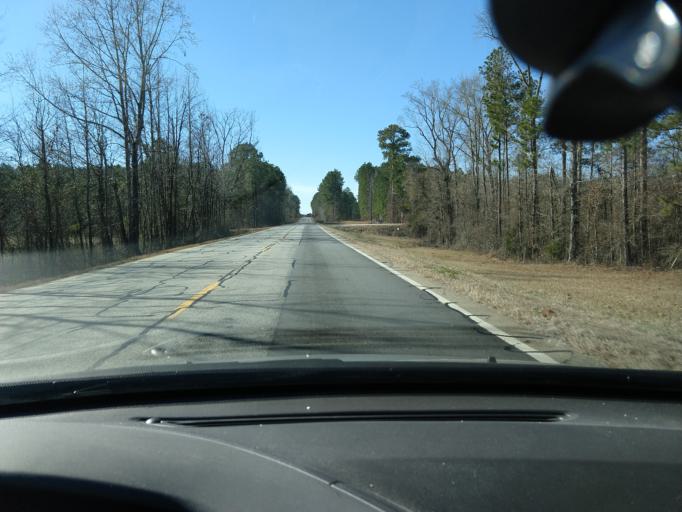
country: US
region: Georgia
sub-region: Jasper County
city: Monticello
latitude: 33.2303
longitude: -83.7366
